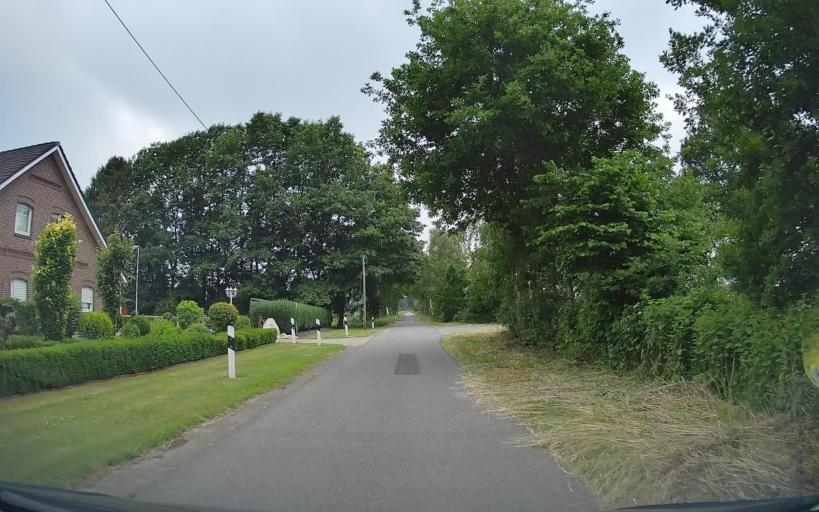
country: DE
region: Lower Saxony
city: Friesoythe
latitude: 53.0122
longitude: 7.8953
